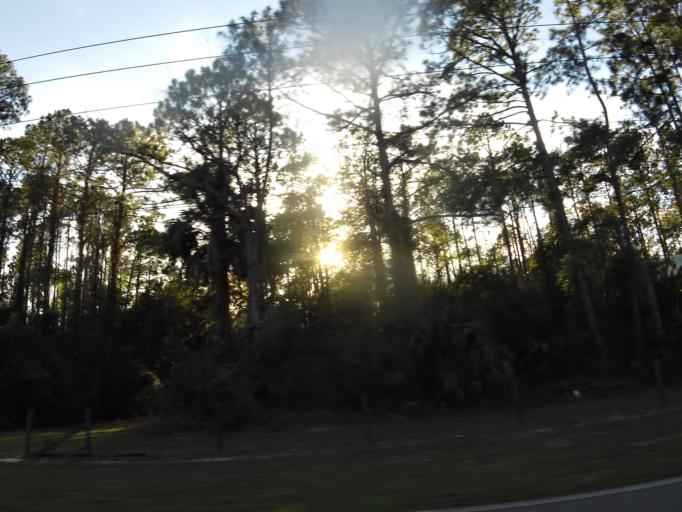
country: US
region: Florida
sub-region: Duval County
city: Jacksonville
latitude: 30.4339
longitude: -81.6037
